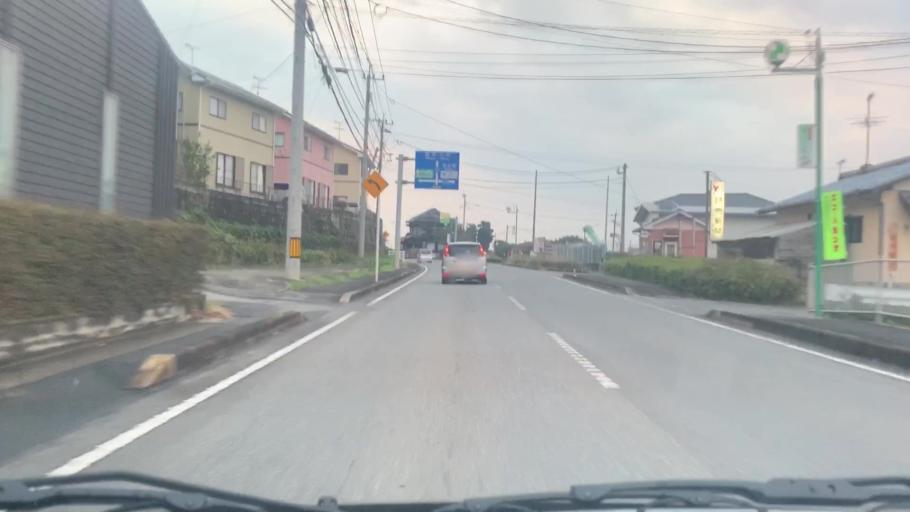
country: JP
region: Saga Prefecture
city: Ureshinomachi-shimojuku
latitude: 33.0385
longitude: 129.9219
